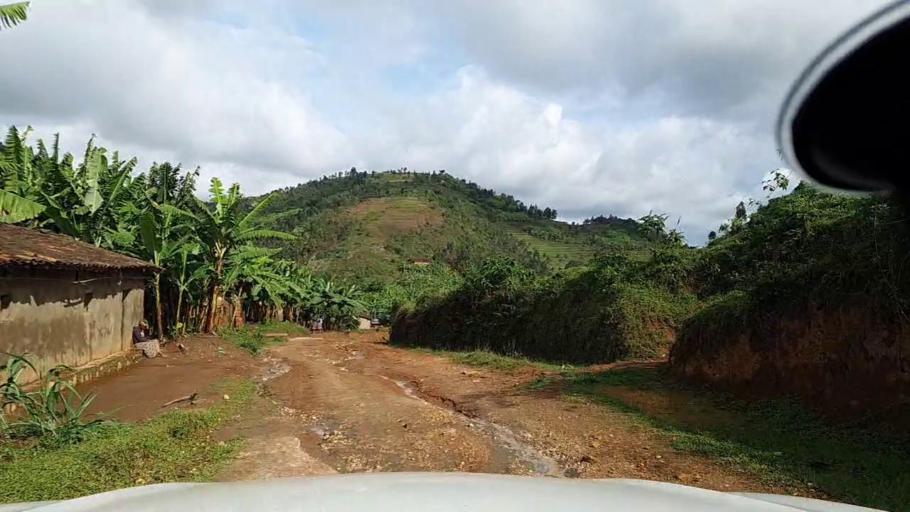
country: RW
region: Western Province
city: Kibuye
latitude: -2.1340
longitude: 29.5032
